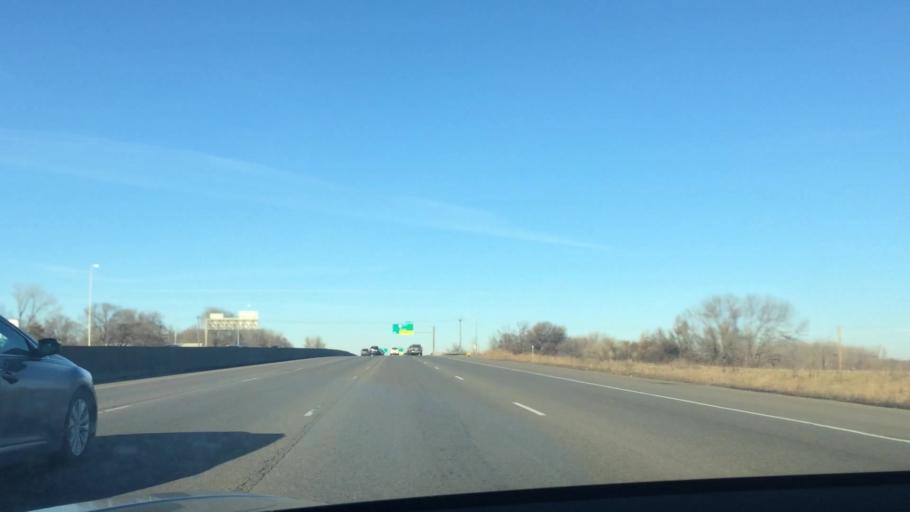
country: US
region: Minnesota
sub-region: Ramsey County
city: Mounds View
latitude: 45.1062
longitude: -93.1882
